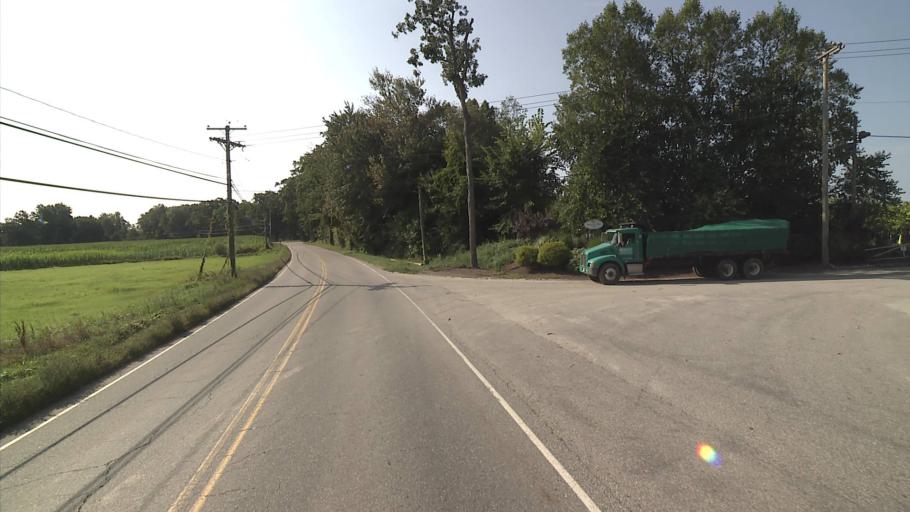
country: US
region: Connecticut
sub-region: Windham County
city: South Windham
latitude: 41.6205
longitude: -72.1980
